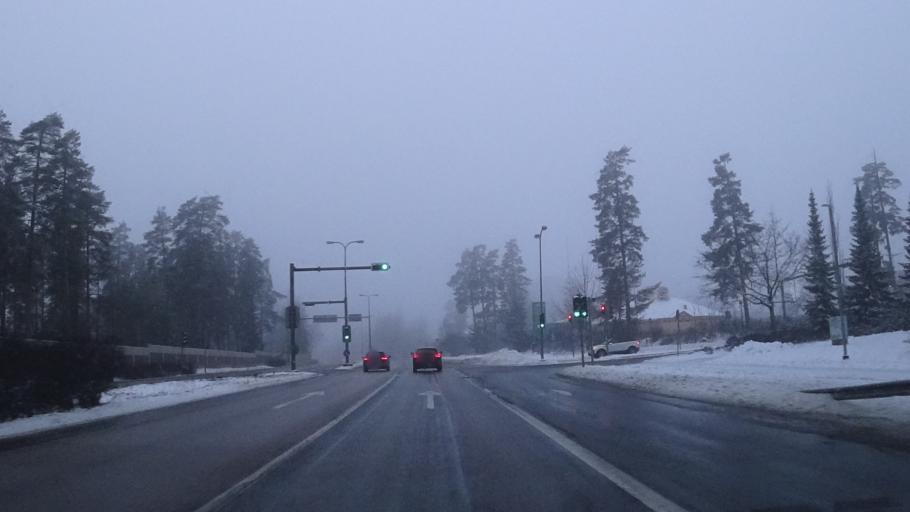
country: FI
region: Paijanne Tavastia
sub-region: Lahti
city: Hollola
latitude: 60.9870
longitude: 25.5175
